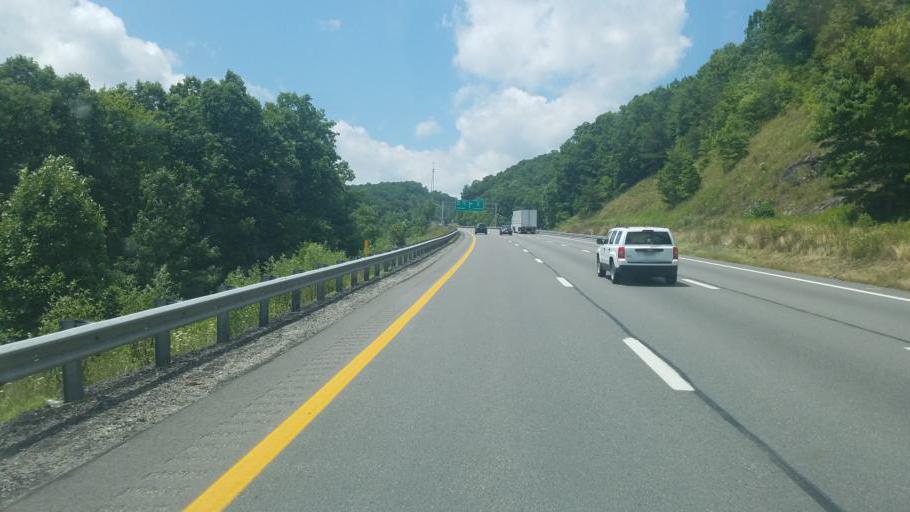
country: US
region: West Virginia
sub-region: Raleigh County
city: Beaver
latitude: 37.7213
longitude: -81.1715
